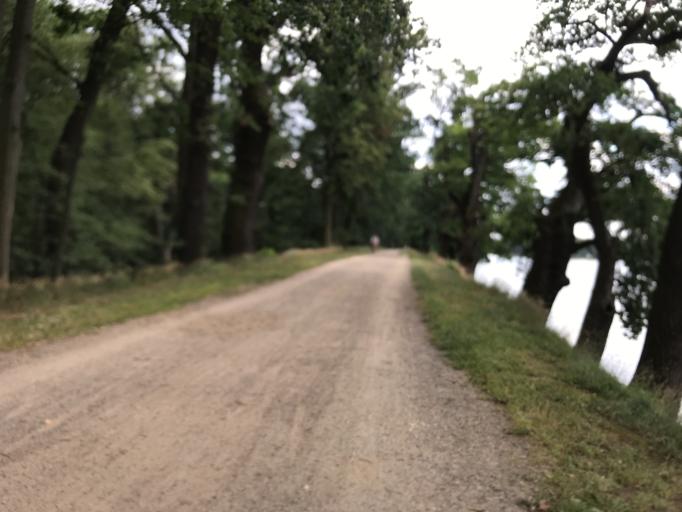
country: CZ
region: Jihocesky
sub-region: Okres Jindrichuv Hradec
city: Trebon
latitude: 48.9921
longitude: 14.7733
